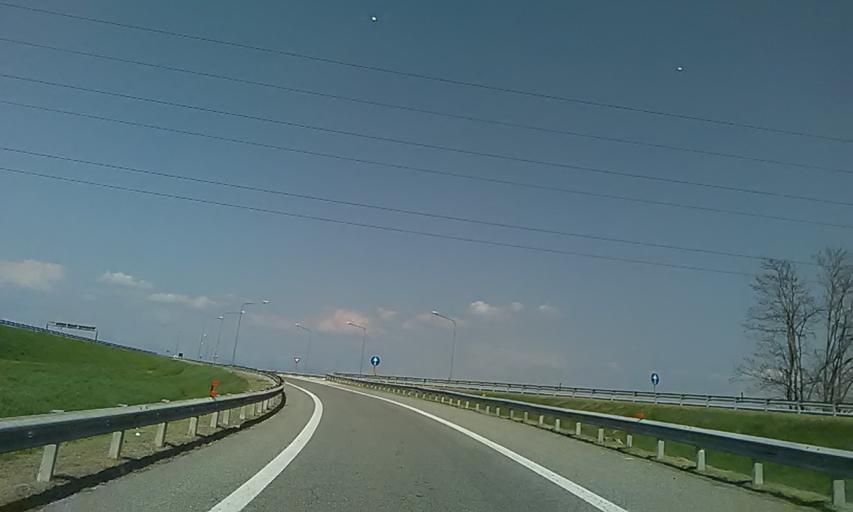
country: IT
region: Piedmont
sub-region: Provincia di Novara
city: Vicolungo
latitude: 45.4688
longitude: 8.4503
